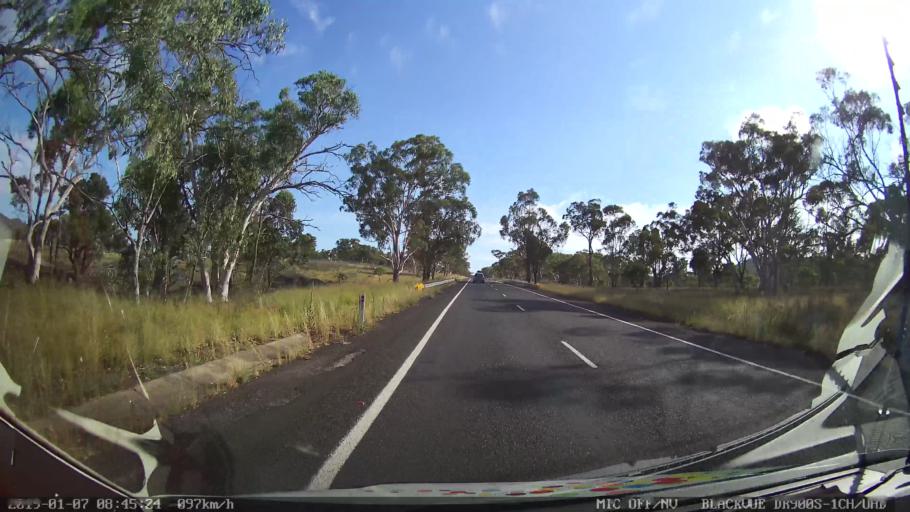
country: AU
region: New South Wales
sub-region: Tamworth Municipality
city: Kootingal
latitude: -30.8197
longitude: 151.2249
